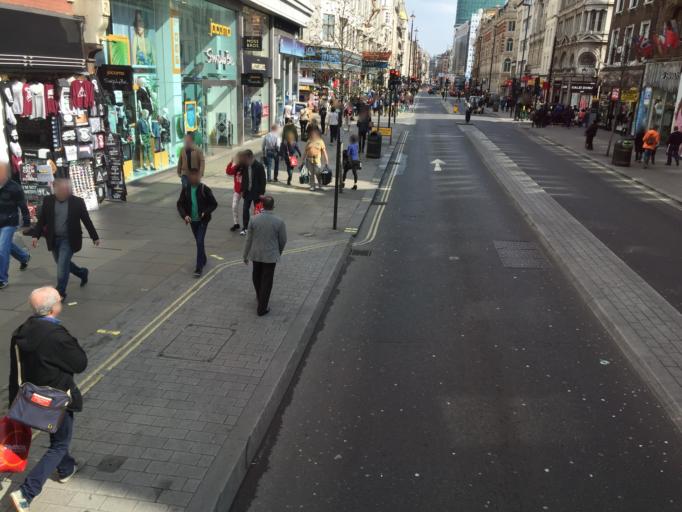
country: GB
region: England
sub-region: Greater London
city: London
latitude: 51.5159
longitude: -0.1376
